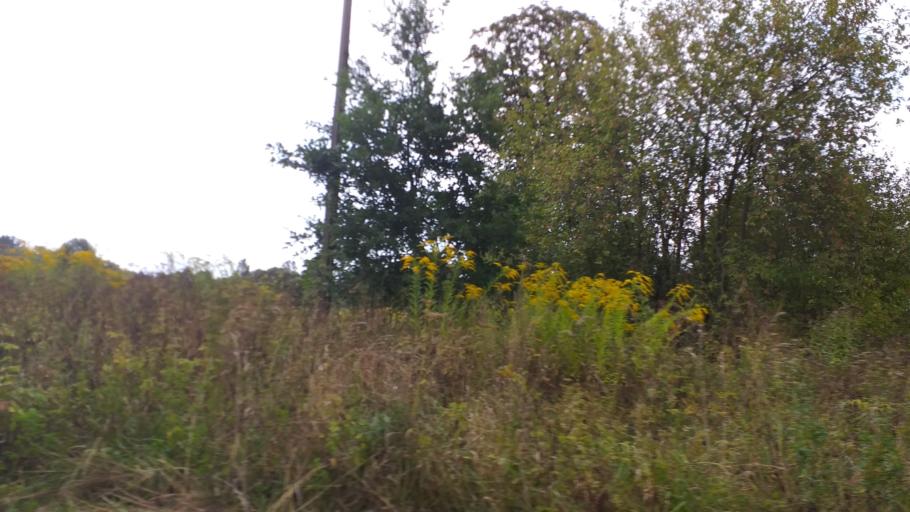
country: PL
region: Lower Silesian Voivodeship
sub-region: Powiat lubanski
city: Lesna
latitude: 51.0460
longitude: 15.2597
